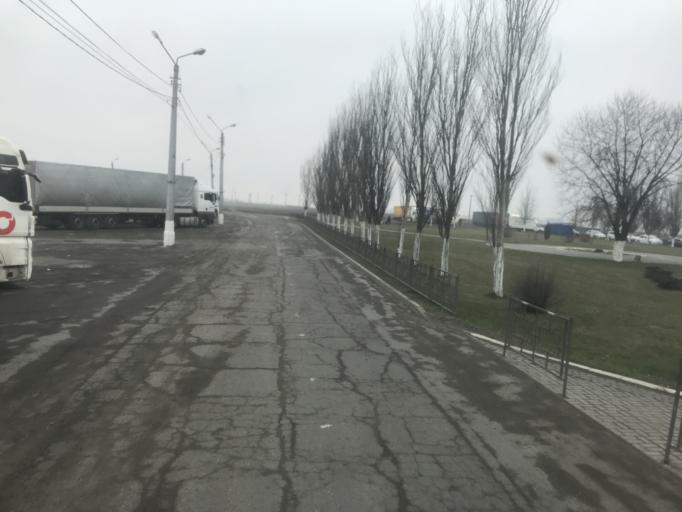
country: RU
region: Volgograd
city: Svetlyy Yar
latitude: 48.4903
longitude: 44.6624
